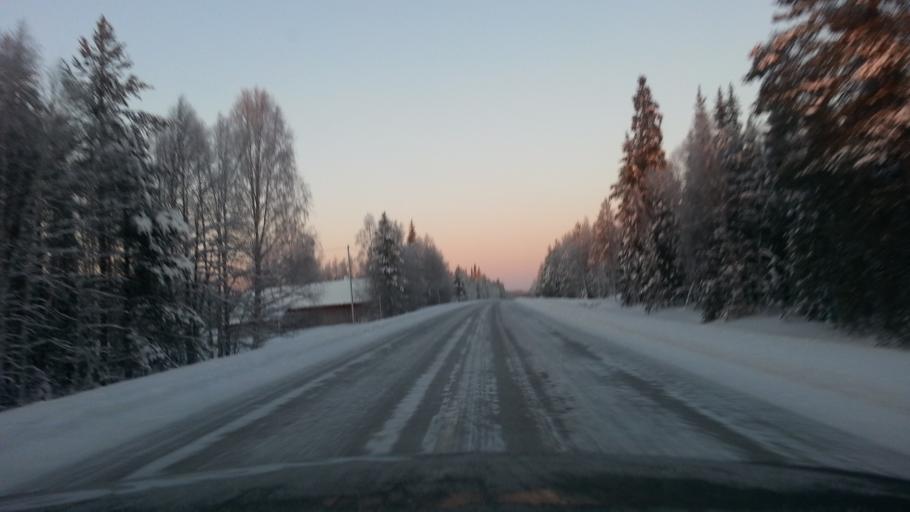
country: FI
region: Lapland
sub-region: Tunturi-Lappi
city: Kittilae
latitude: 67.2185
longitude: 24.9240
